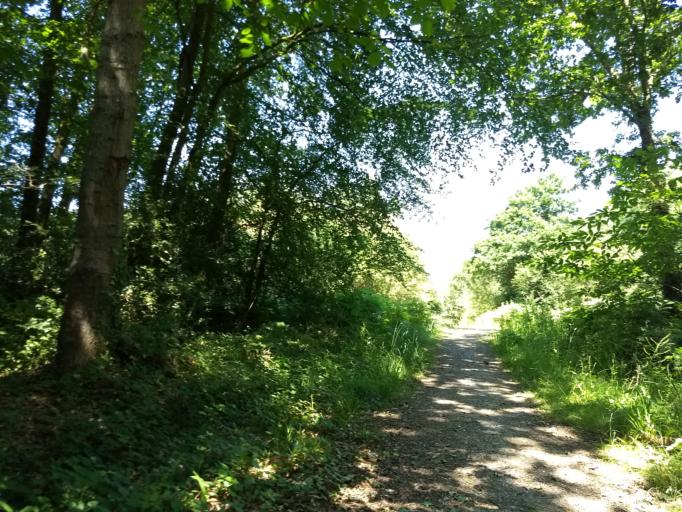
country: GB
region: England
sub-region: Isle of Wight
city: Northwood
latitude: 50.7078
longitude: -1.3350
